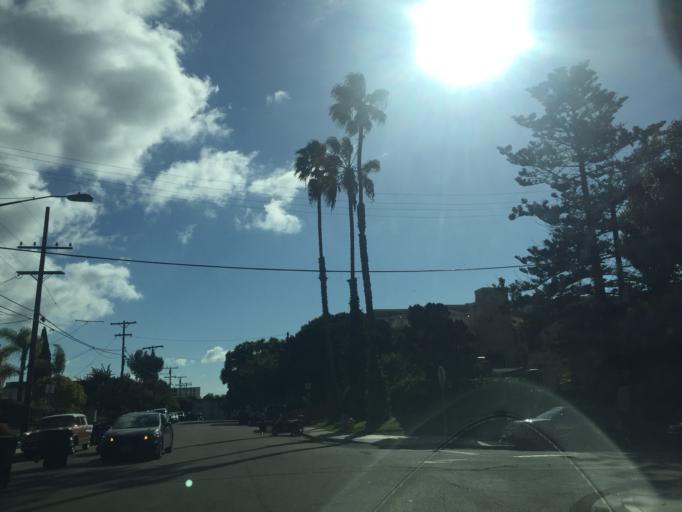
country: US
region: California
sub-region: San Diego County
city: La Jolla
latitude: 32.7926
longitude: -117.2425
